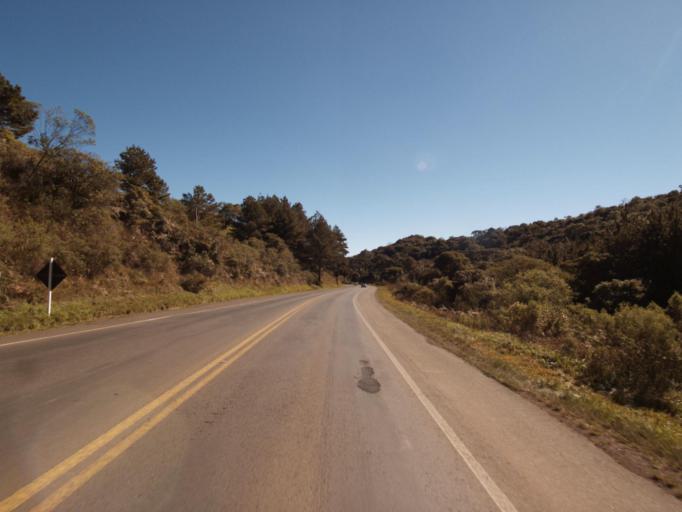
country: BR
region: Santa Catarina
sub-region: Concordia
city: Concordia
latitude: -26.8874
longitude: -51.9991
